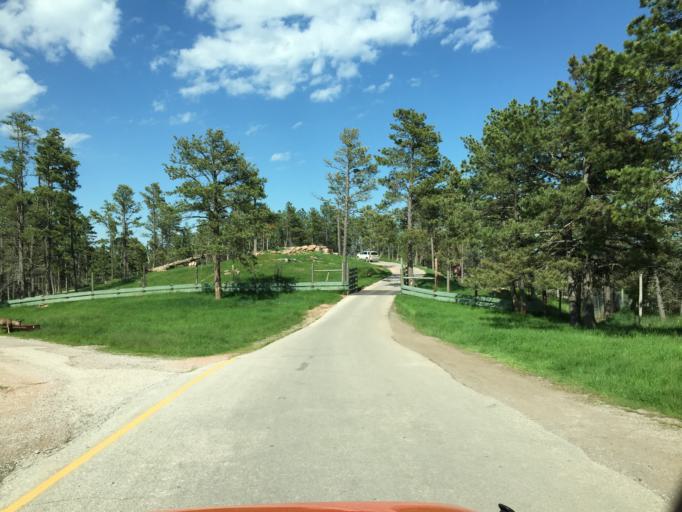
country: US
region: South Dakota
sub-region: Pennington County
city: Colonial Pine Hills
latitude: 43.9797
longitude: -103.2952
